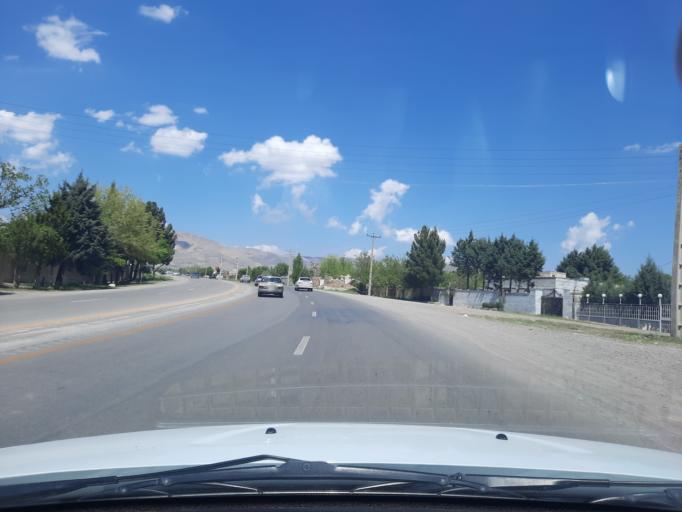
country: IR
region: Qazvin
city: Alvand
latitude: 36.3009
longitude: 50.1432
